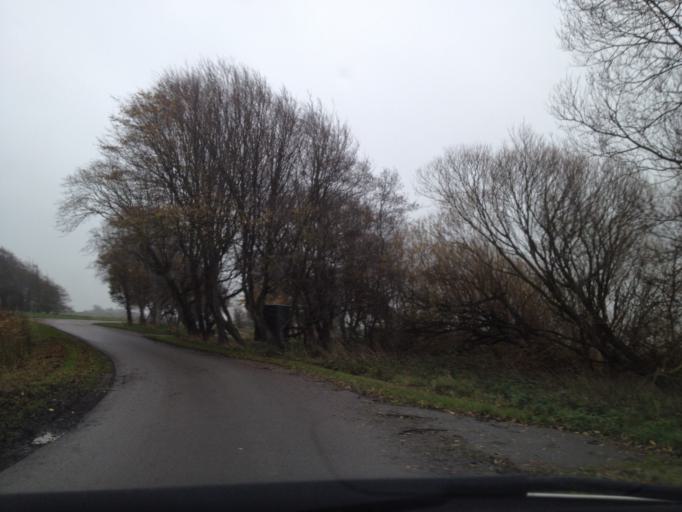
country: DE
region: Schleswig-Holstein
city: Aventoft
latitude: 55.0210
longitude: 8.7529
